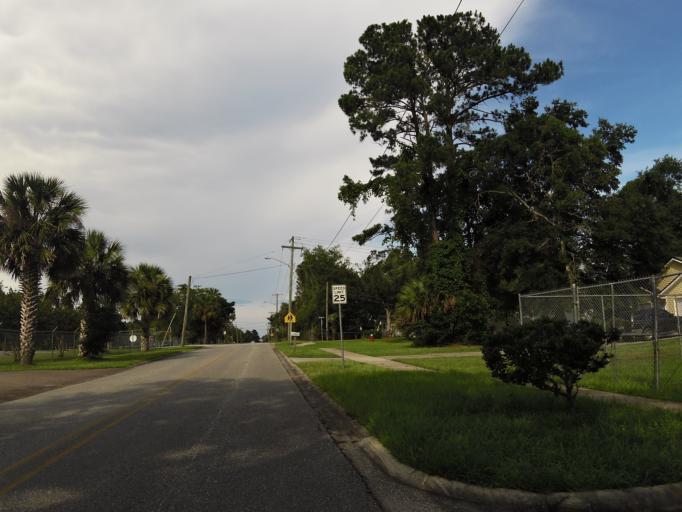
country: US
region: Florida
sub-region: Clay County
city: Green Cove Springs
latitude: 29.9934
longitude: -81.6976
